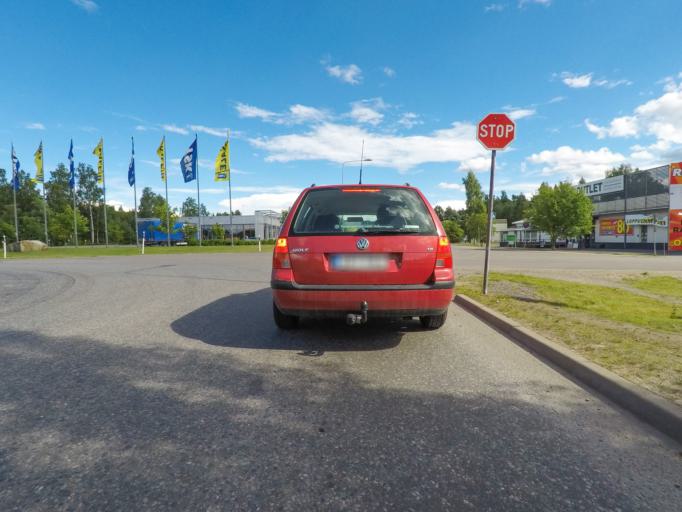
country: FI
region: Paijanne Tavastia
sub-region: Lahti
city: Heinola
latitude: 61.2320
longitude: 26.0456
